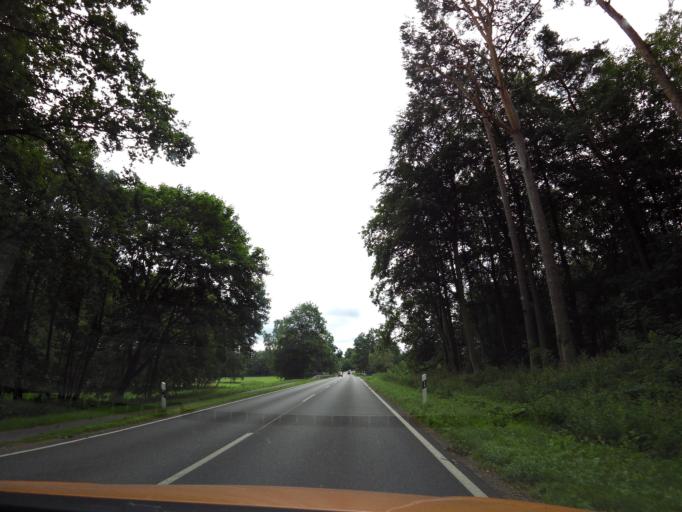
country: DE
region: Mecklenburg-Vorpommern
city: Muhl Rosin
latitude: 53.7814
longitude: 12.2382
